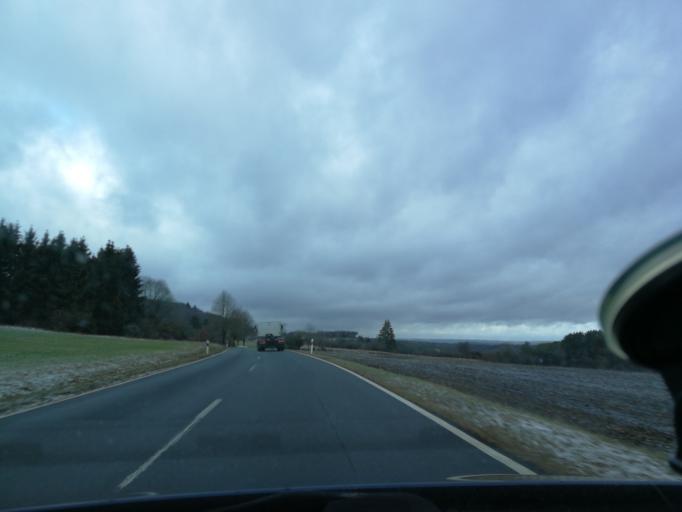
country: DE
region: Rheinland-Pfalz
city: Oberehe-Stroheich
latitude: 50.2967
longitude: 6.7579
